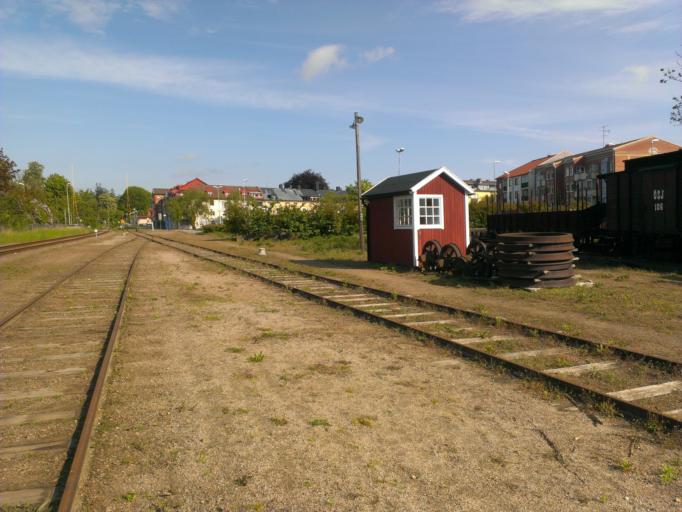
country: SE
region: Skane
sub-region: Kristianstads Kommun
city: Kristianstad
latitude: 56.0235
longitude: 14.1607
